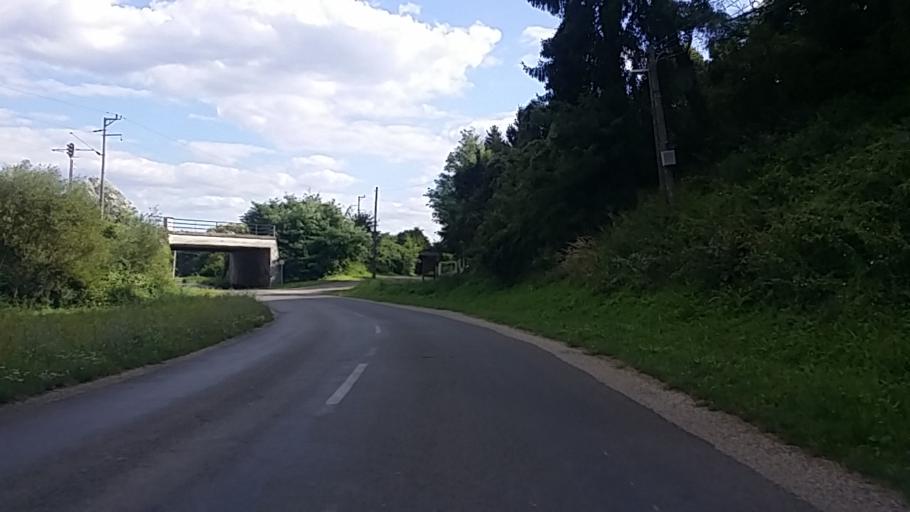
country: HU
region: Baranya
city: Sasd
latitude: 46.1959
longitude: 18.0827
